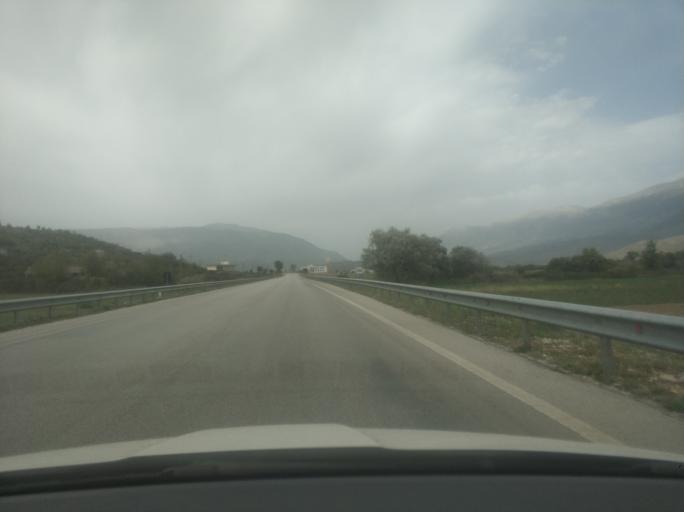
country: AL
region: Gjirokaster
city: Gjirokaster
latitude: 40.1132
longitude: 20.1203
